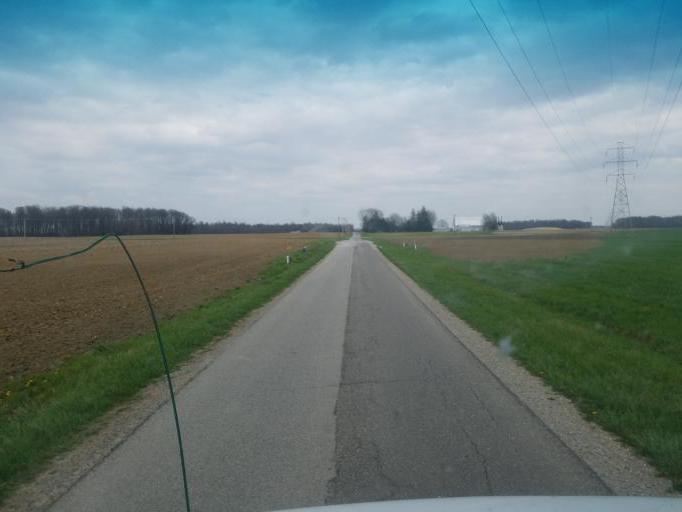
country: US
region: Ohio
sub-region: Crawford County
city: Bucyrus
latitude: 40.9794
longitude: -82.9807
